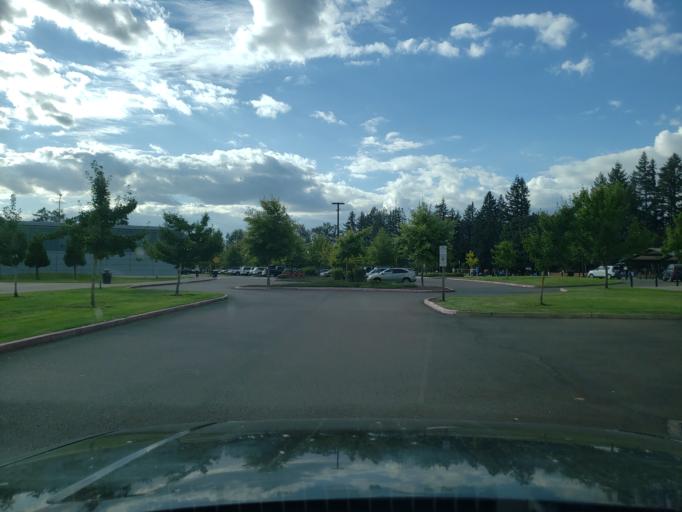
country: US
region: Oregon
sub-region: Marion County
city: Keizer
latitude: 44.9698
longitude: -123.0319
